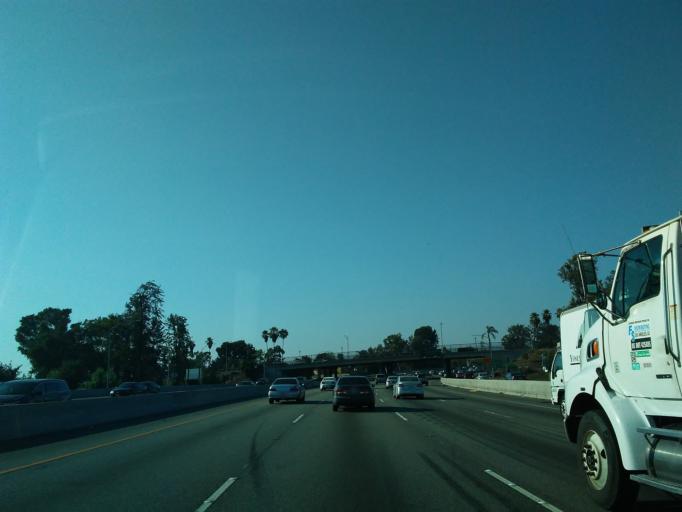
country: US
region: California
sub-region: Los Angeles County
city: Cudahy
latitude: 33.9290
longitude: -118.1787
